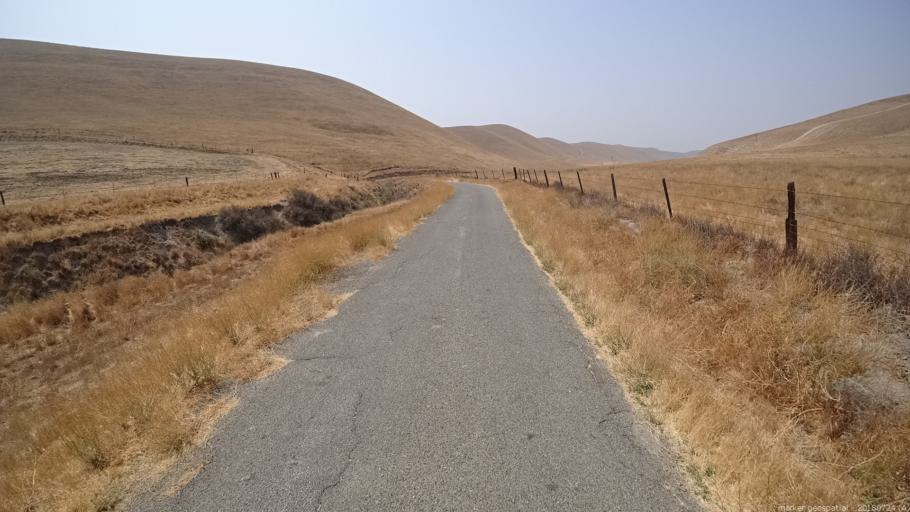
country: US
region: California
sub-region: Monterey County
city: King City
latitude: 36.1907
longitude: -120.9665
